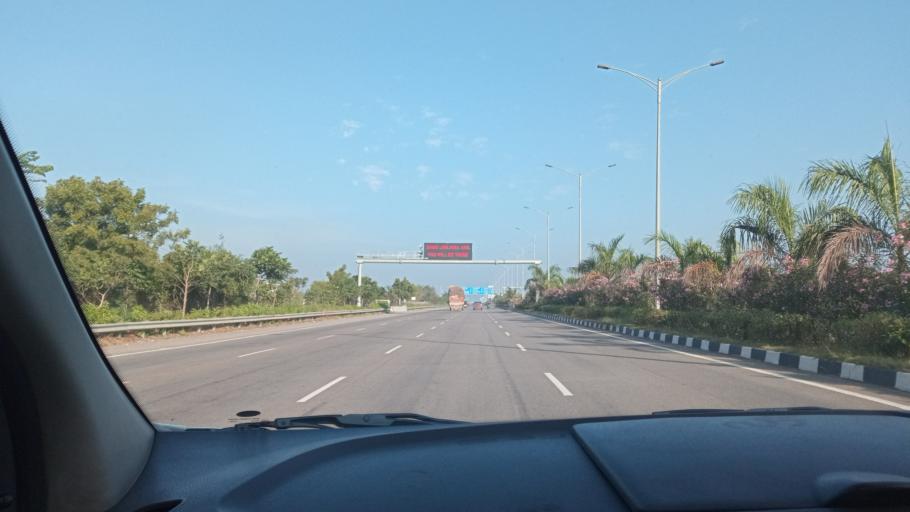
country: IN
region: Telangana
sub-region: Hyderabad
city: Hyderabad
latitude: 17.3339
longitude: 78.3693
